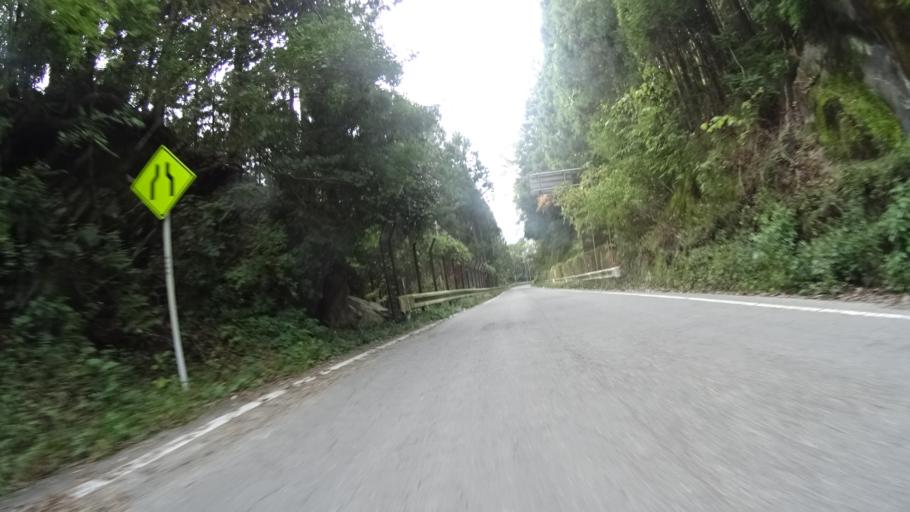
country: JP
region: Yamanashi
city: Uenohara
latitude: 35.6806
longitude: 139.0987
